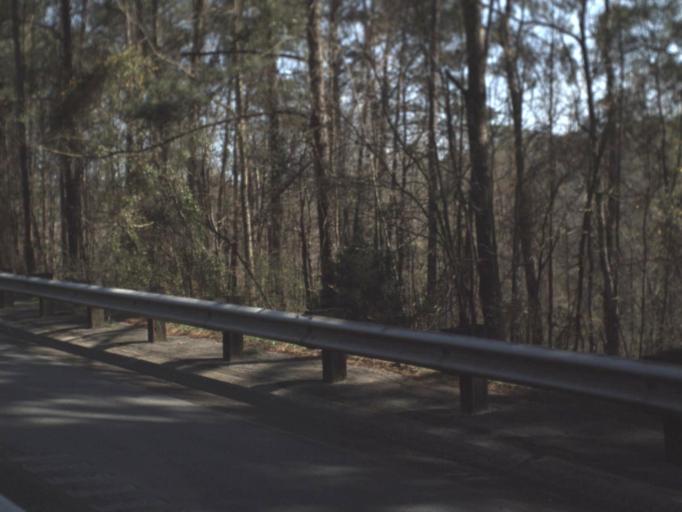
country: US
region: Florida
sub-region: Gadsden County
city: Chattahoochee
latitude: 30.6297
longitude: -84.8626
